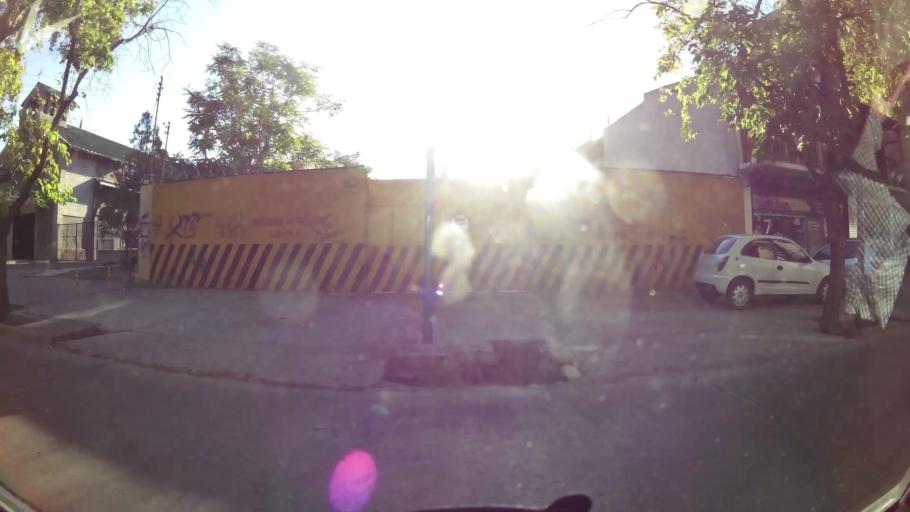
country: AR
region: Mendoza
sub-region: Departamento de Godoy Cruz
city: Godoy Cruz
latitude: -32.9058
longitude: -68.8517
